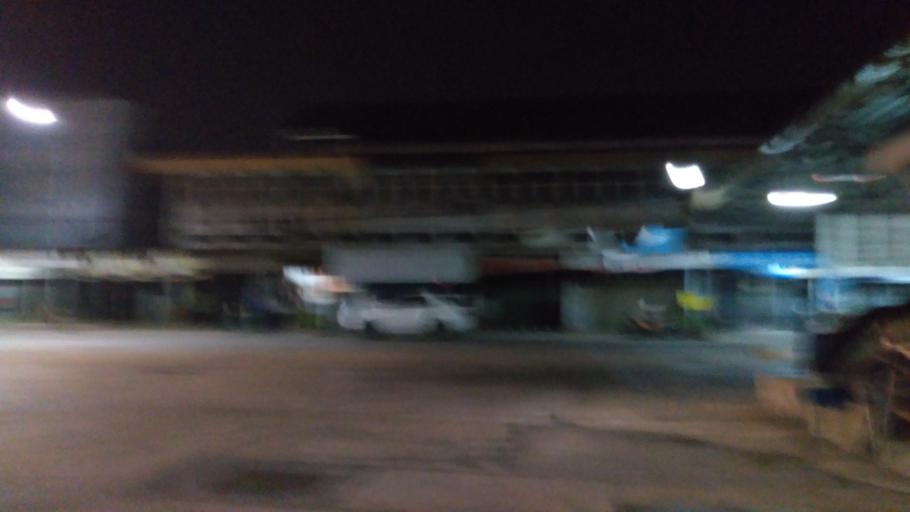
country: TH
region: Khon Kaen
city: Khon Kaen
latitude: 16.4397
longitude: 102.8332
